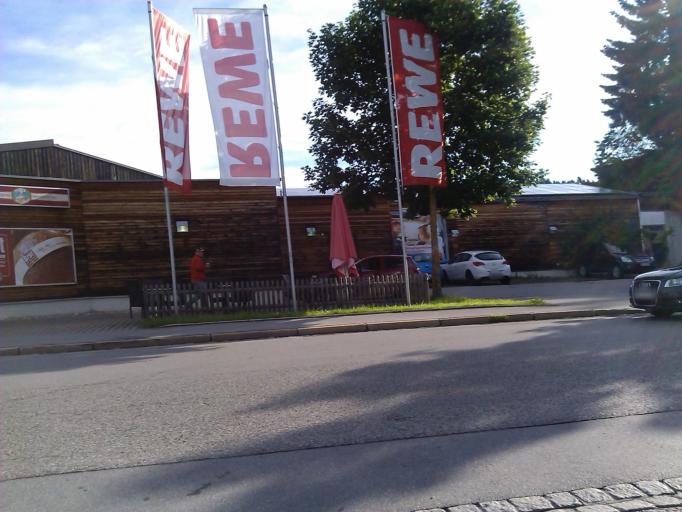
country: DE
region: Bavaria
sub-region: Swabia
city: Fuessen
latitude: 47.5725
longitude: 10.6851
